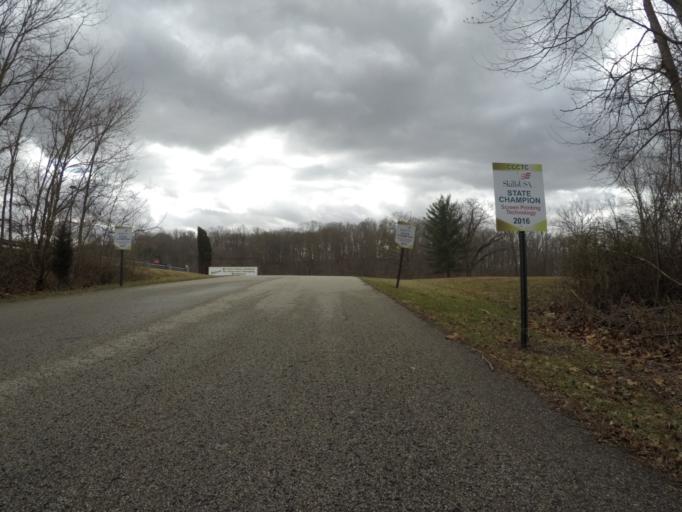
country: US
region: West Virginia
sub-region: Cabell County
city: Pea Ridge
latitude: 38.4028
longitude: -82.3736
